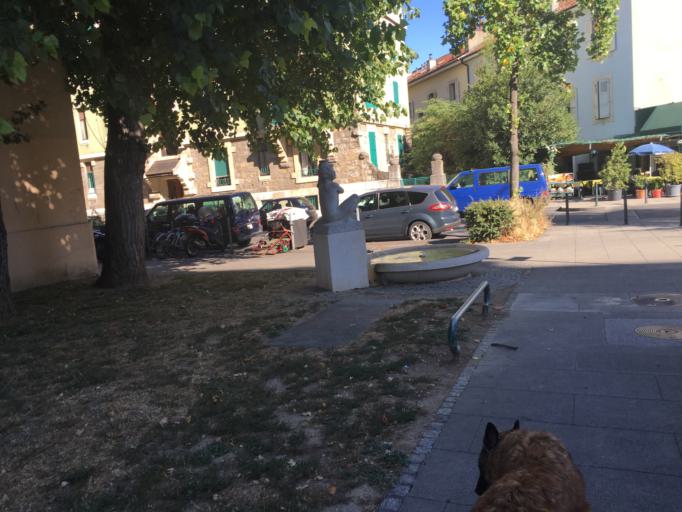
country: CH
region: Geneva
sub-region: Geneva
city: Geneve
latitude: 46.2113
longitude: 6.1372
